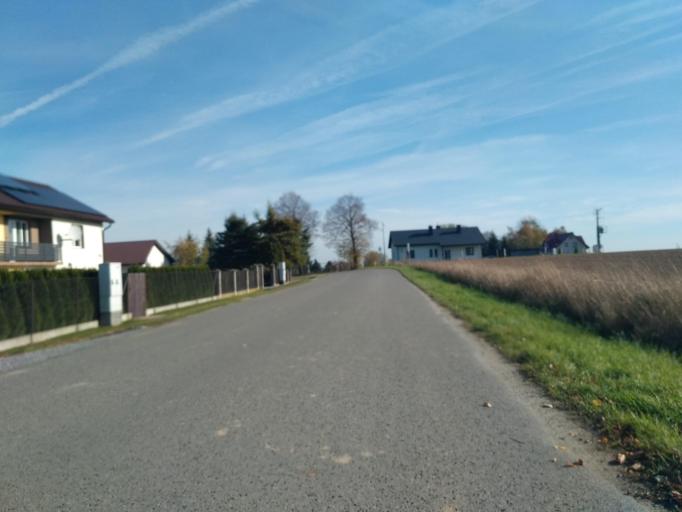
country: PL
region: Subcarpathian Voivodeship
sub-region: Powiat ropczycko-sedziszowski
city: Iwierzyce
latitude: 50.0007
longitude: 21.7347
